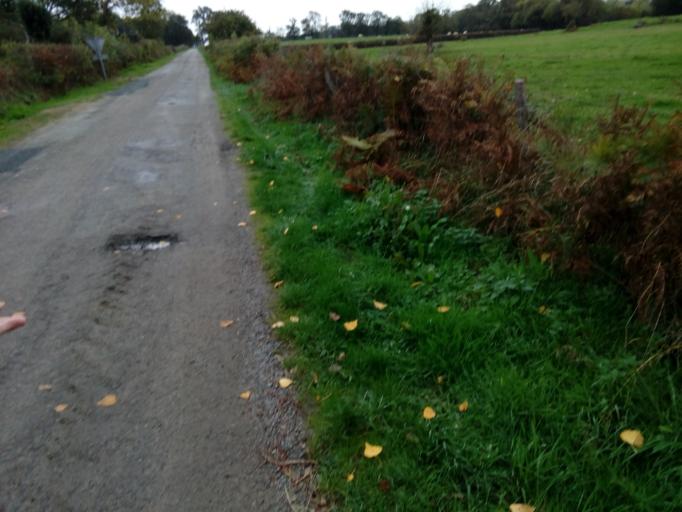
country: FR
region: Limousin
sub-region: Departement de la Creuse
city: Sainte-Feyre
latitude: 46.1793
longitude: 1.9114
